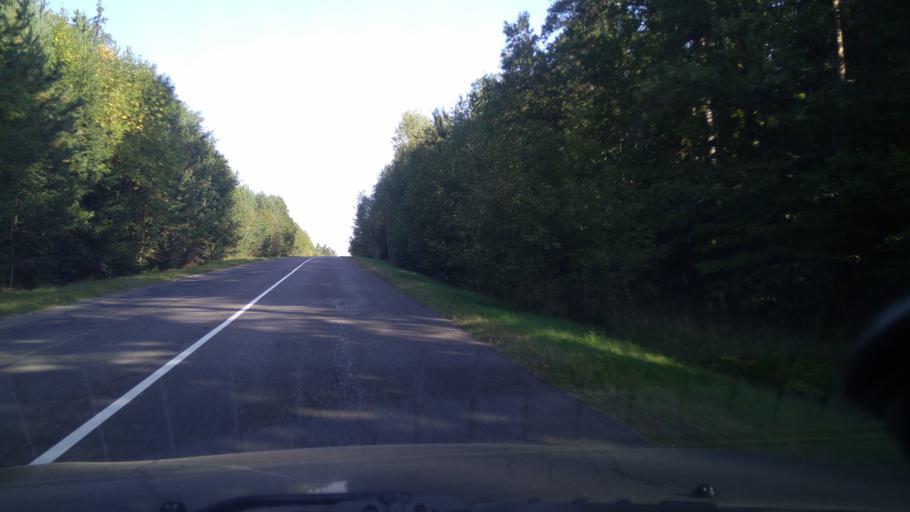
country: BY
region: Minsk
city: Rakaw
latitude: 53.9863
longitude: 27.0418
